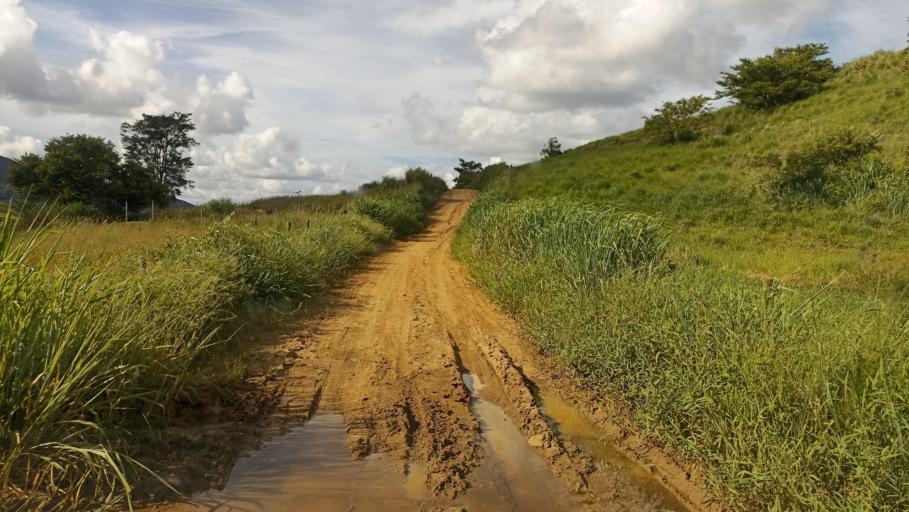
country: BR
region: Minas Gerais
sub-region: Almenara
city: Almenara
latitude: -16.6279
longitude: -40.4621
